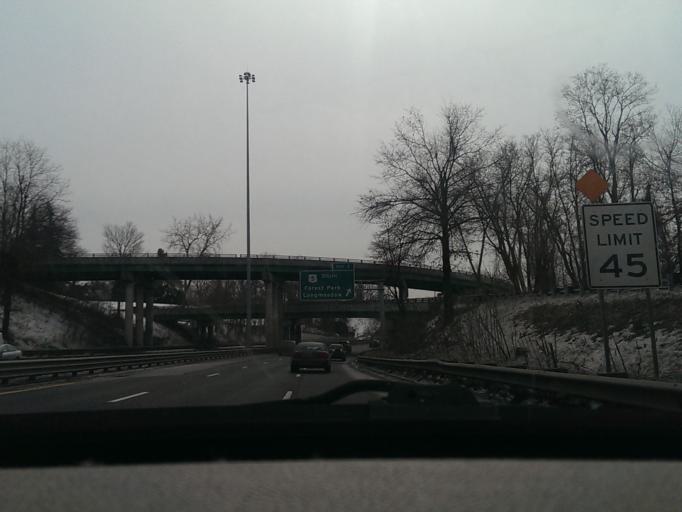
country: US
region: Massachusetts
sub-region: Hampden County
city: Springfield
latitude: 42.0790
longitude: -72.5797
